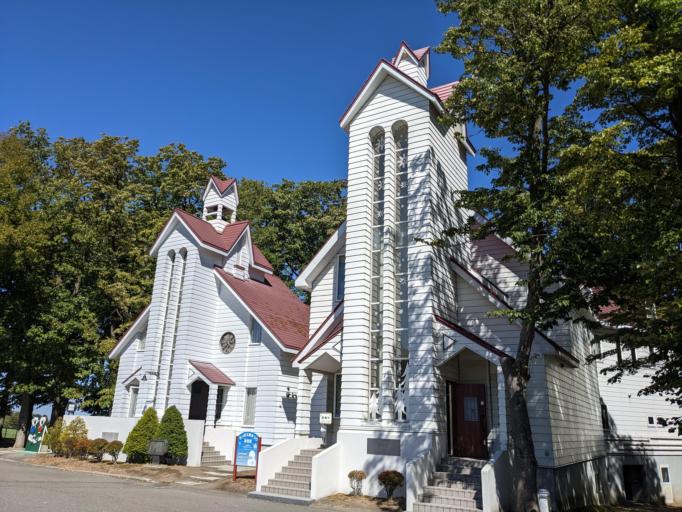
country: JP
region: Hokkaido
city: Sapporo
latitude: 42.9987
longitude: 141.3954
